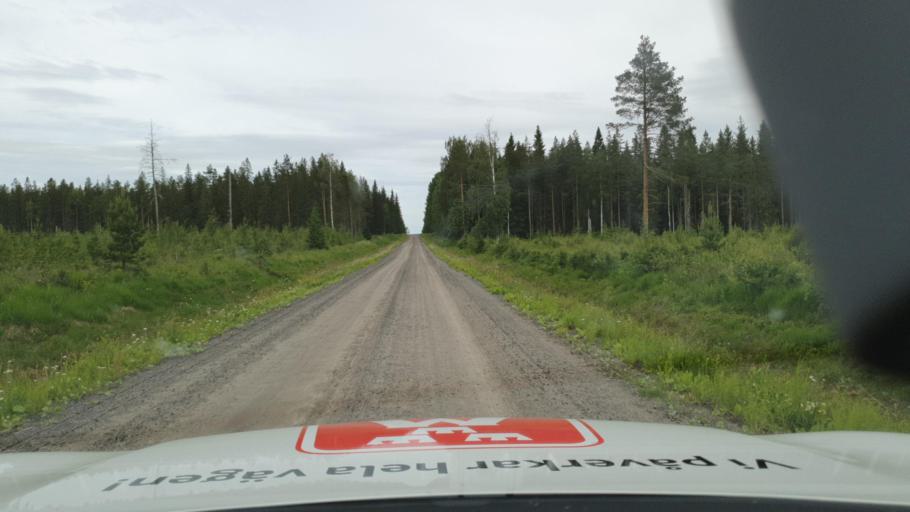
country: SE
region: Vaesterbotten
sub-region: Skelleftea Kommun
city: Burtraesk
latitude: 64.3746
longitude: 20.6156
